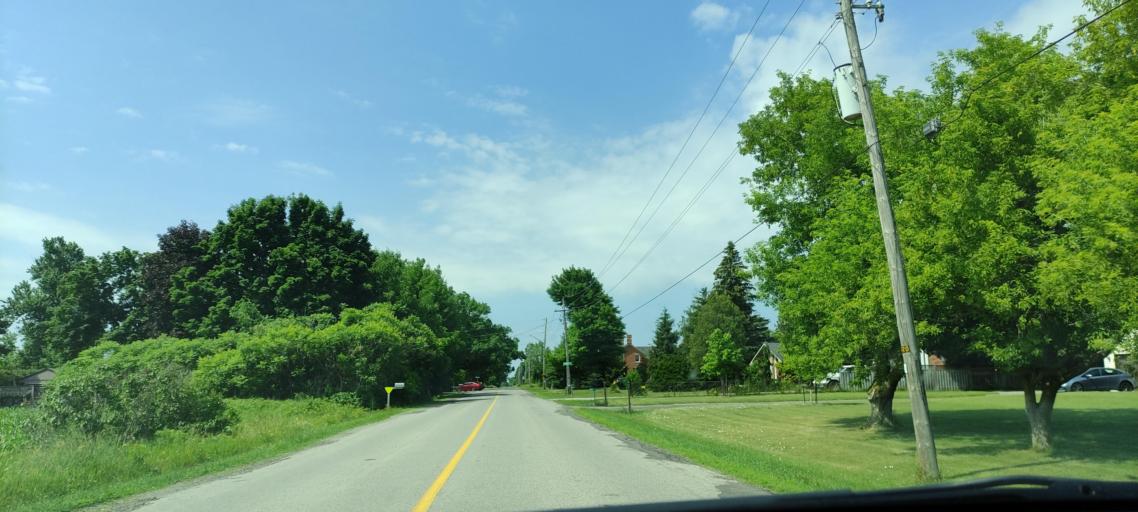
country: CA
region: Ontario
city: Burlington
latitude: 43.3690
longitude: -79.9533
